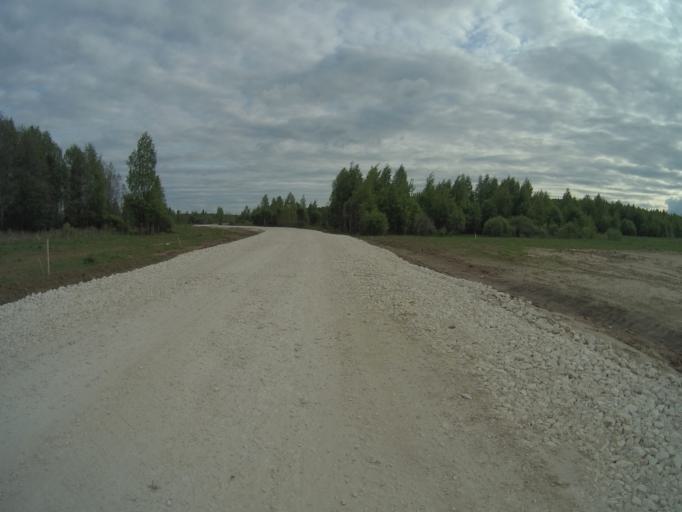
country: RU
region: Vladimir
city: Raduzhnyy
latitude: 56.0107
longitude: 40.3883
